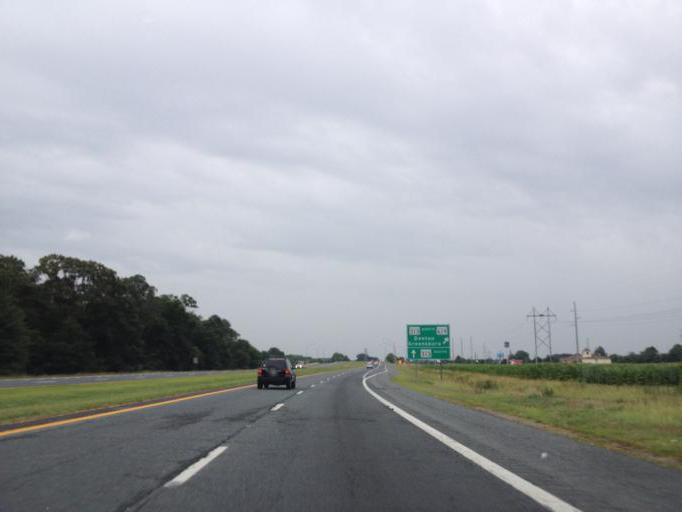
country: US
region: Maryland
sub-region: Caroline County
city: Denton
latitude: 38.8964
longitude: -75.8278
